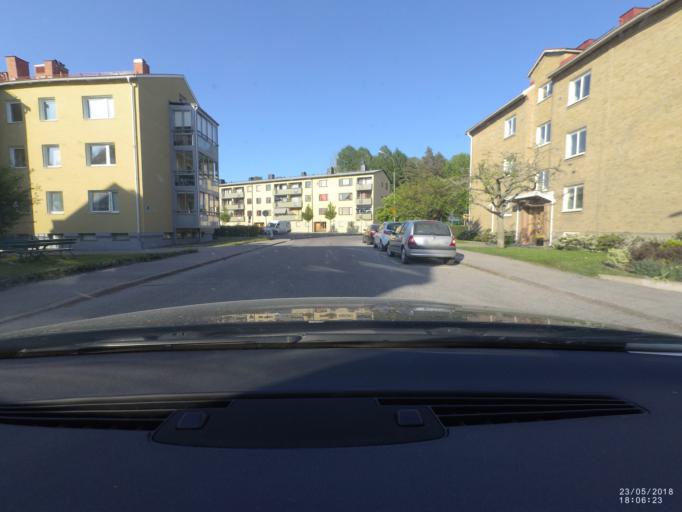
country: SE
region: Soedermanland
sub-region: Nykopings Kommun
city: Nykoping
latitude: 58.7522
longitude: 17.0279
